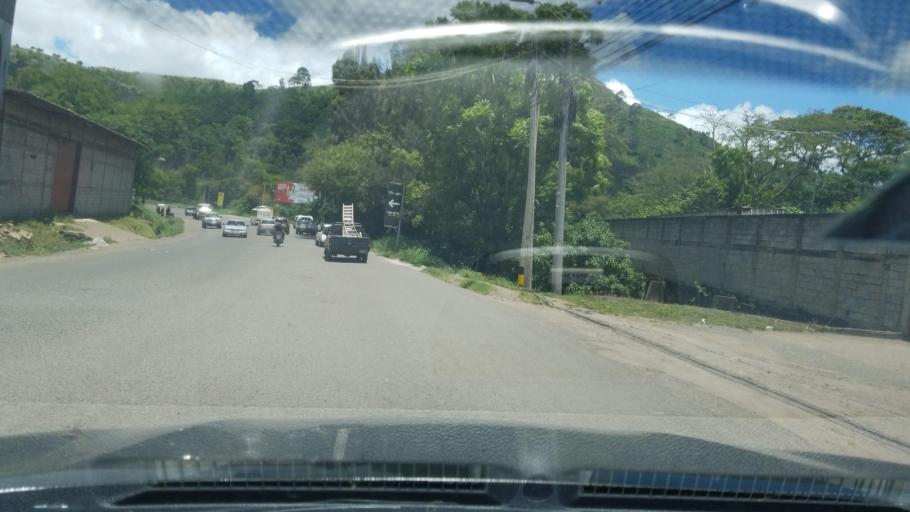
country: HN
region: Francisco Morazan
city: Rio Abajo
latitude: 14.1359
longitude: -87.2340
